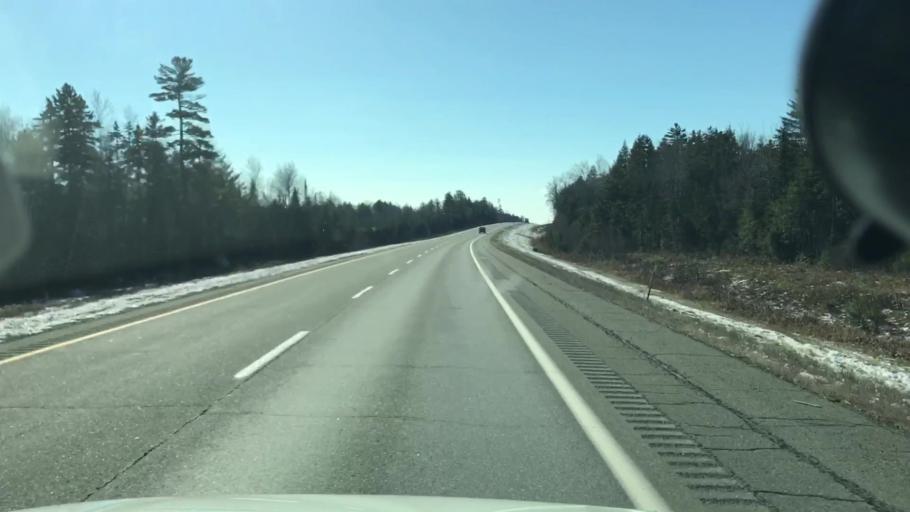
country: US
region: Maine
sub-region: Penobscot County
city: Howland
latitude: 45.2871
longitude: -68.6674
